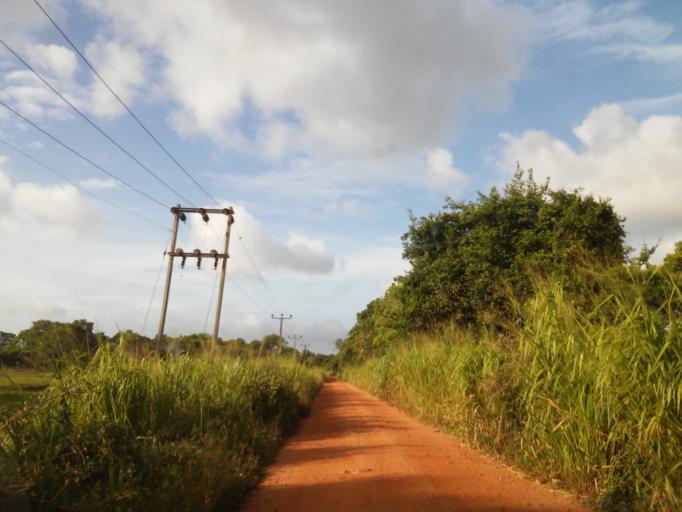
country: LK
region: Central
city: Sigiriya
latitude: 8.1693
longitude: 80.6849
